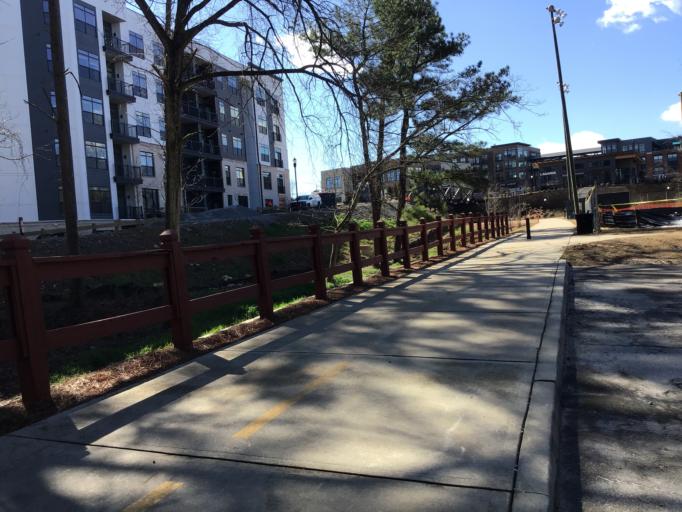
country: US
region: Georgia
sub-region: DeKalb County
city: Chamblee
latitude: 33.8905
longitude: -84.3139
